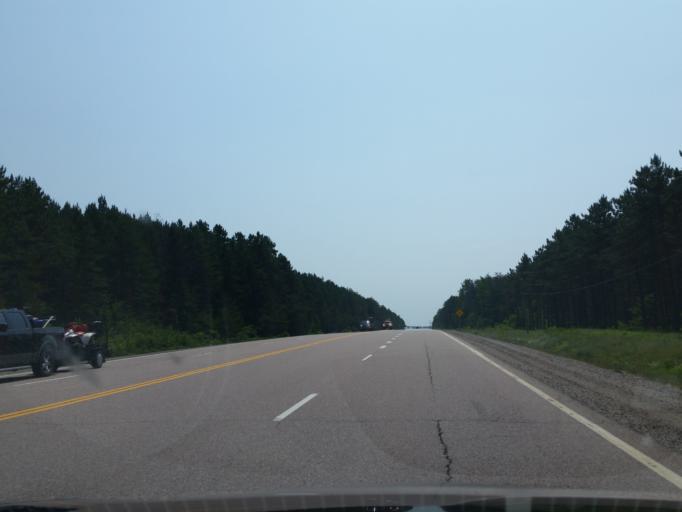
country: CA
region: Ontario
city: Deep River
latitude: 46.1773
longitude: -77.8378
